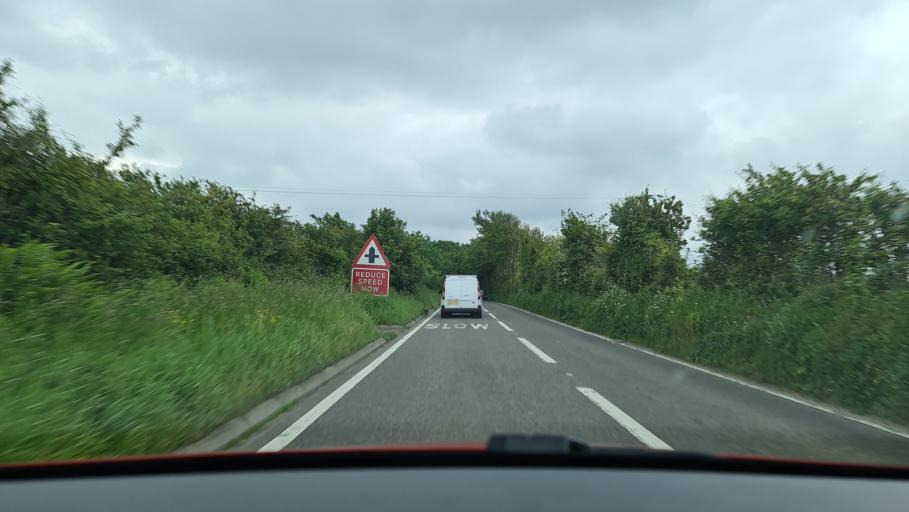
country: GB
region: England
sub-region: Cornwall
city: Camelford
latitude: 50.6295
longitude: -4.6663
